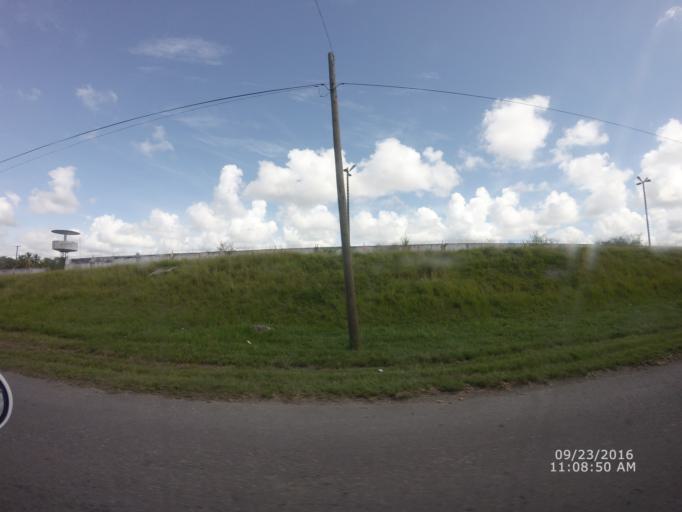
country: CU
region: La Habana
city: Arroyo Naranjo
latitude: 23.0157
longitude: -82.2360
